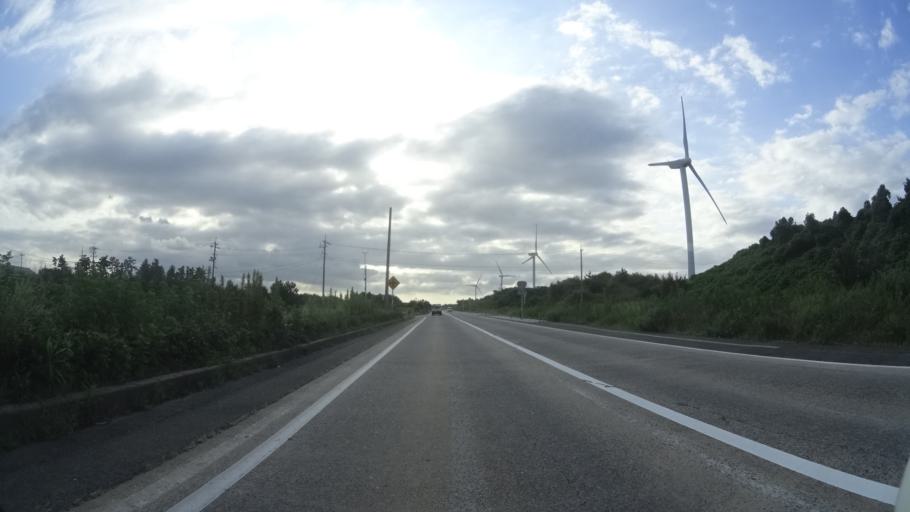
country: JP
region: Tottori
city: Kurayoshi
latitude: 35.4986
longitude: 133.8060
